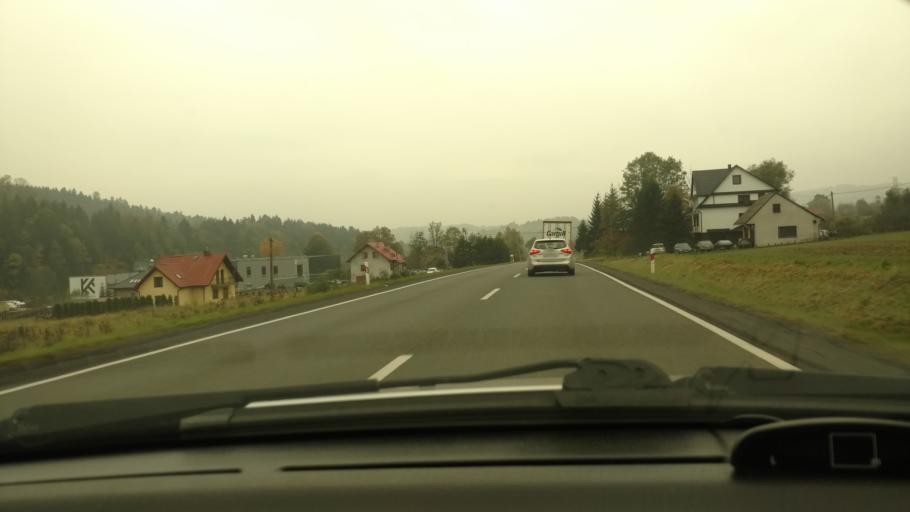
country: PL
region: Lesser Poland Voivodeship
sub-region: Powiat nowosadecki
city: Kamionka Wielka
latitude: 49.6171
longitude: 20.8022
